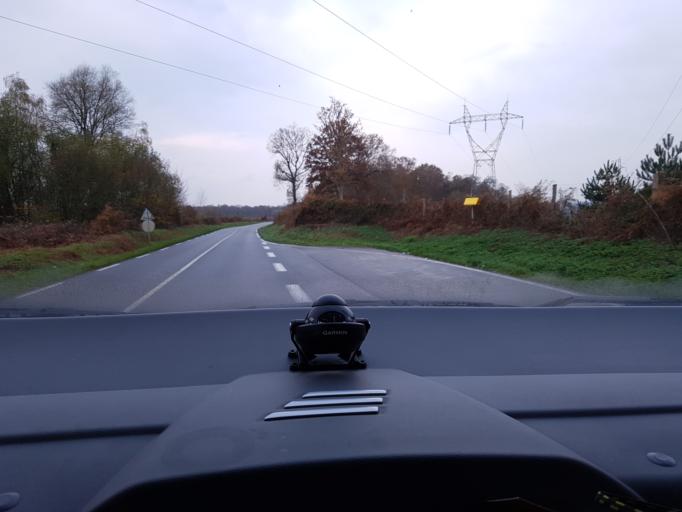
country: FR
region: Haute-Normandie
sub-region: Departement de la Seine-Maritime
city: Saint-Pierre-de-Varengeville
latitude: 49.4953
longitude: 0.9042
